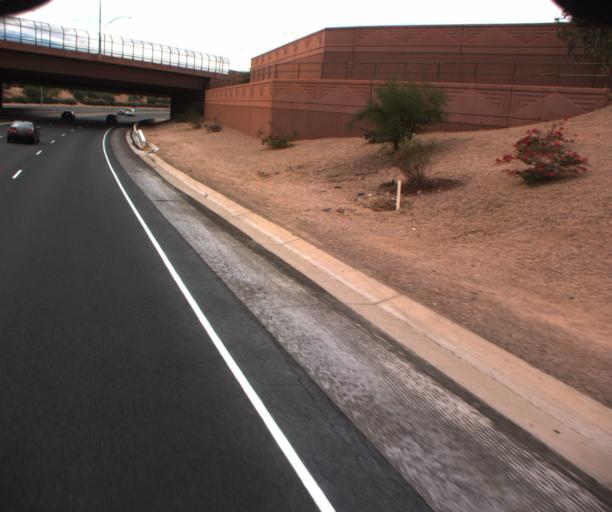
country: US
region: Arizona
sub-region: Maricopa County
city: Mesa
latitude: 33.4687
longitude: -111.7828
